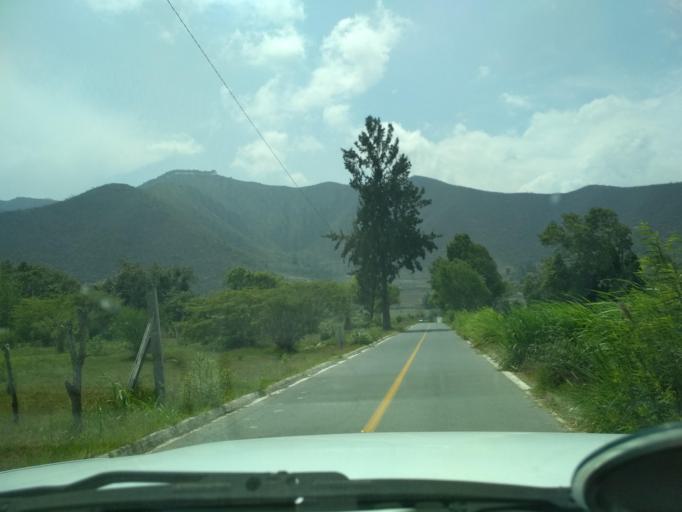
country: MX
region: Veracruz
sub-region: Nogales
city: Taza de Agua Ojo Zarco
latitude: 18.7745
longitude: -97.2173
